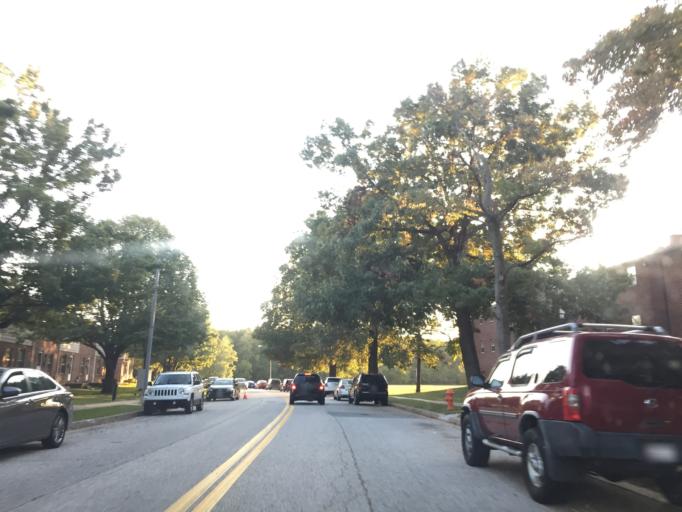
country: US
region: Maryland
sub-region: Baltimore County
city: Essex
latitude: 39.2955
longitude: -76.4467
